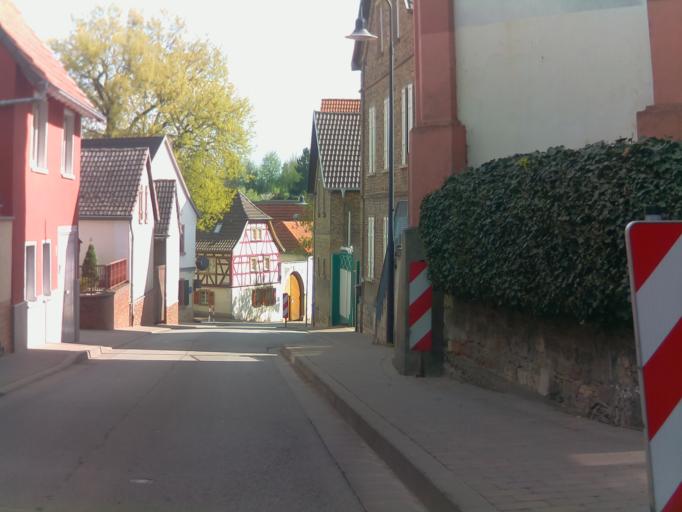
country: DE
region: Rheinland-Pfalz
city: Mommenheim
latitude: 49.8825
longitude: 8.2659
